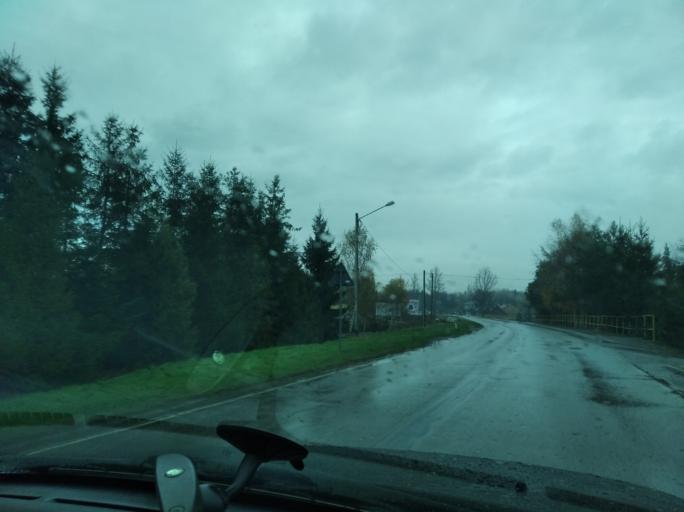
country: PL
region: Subcarpathian Voivodeship
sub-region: Powiat lancucki
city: Albigowa
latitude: 50.0375
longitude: 22.2302
